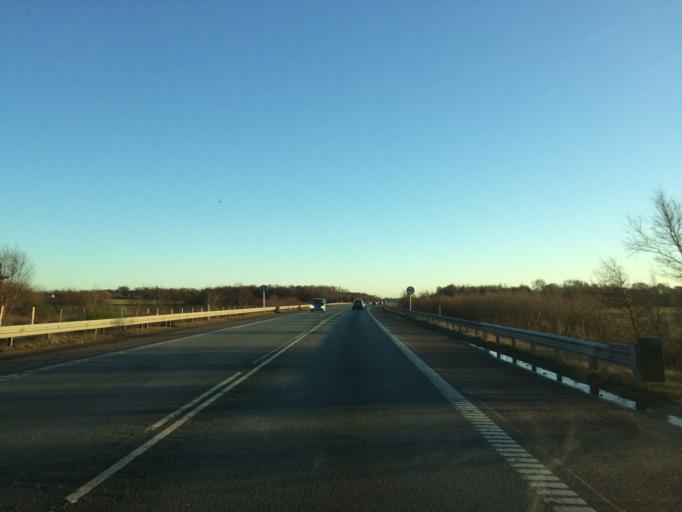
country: DK
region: Central Jutland
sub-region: Herning Kommune
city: Herning
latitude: 56.1659
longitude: 9.0010
